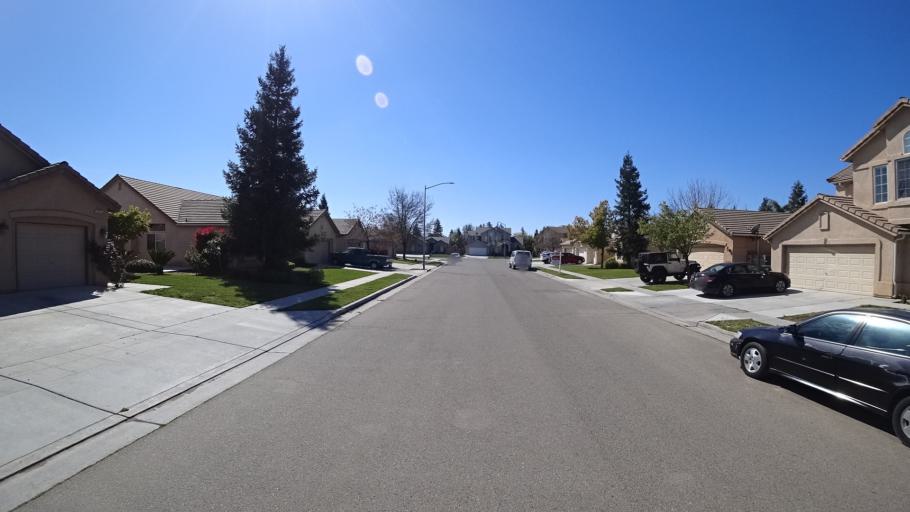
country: US
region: California
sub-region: Fresno County
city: Biola
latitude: 36.8166
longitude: -119.9027
